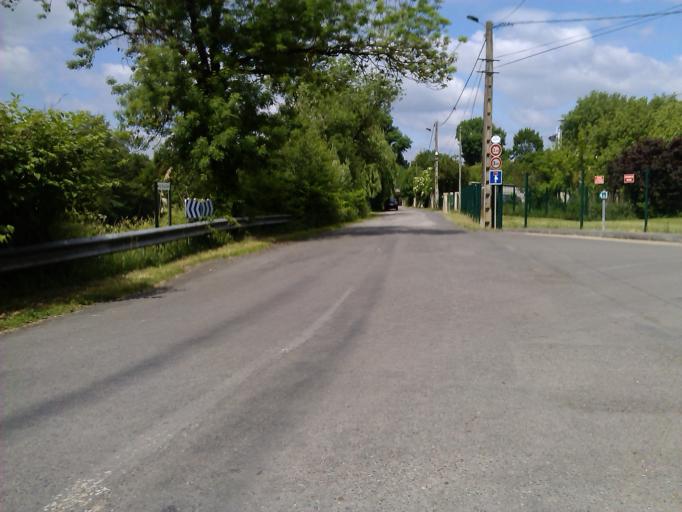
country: FR
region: Poitou-Charentes
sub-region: Departement de la Charente
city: Angouleme
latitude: 45.6565
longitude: 0.1438
